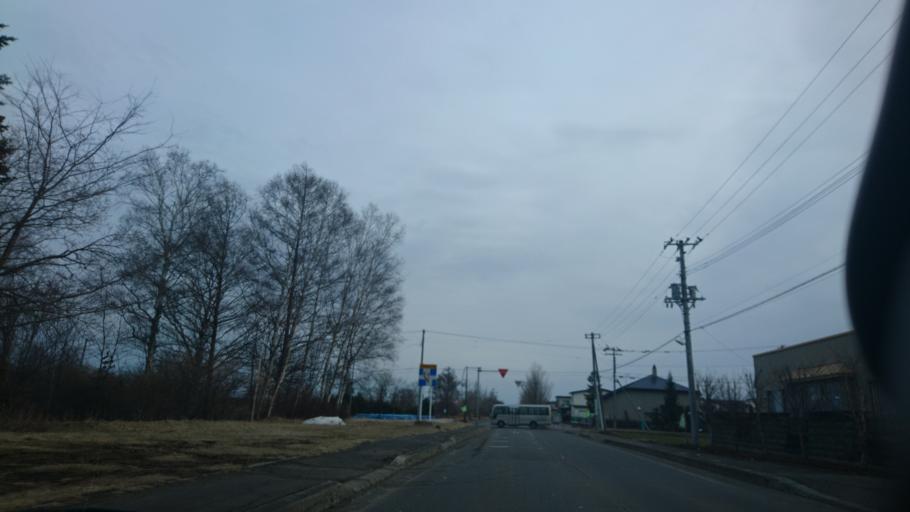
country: JP
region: Hokkaido
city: Otofuke
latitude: 42.9725
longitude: 143.1987
